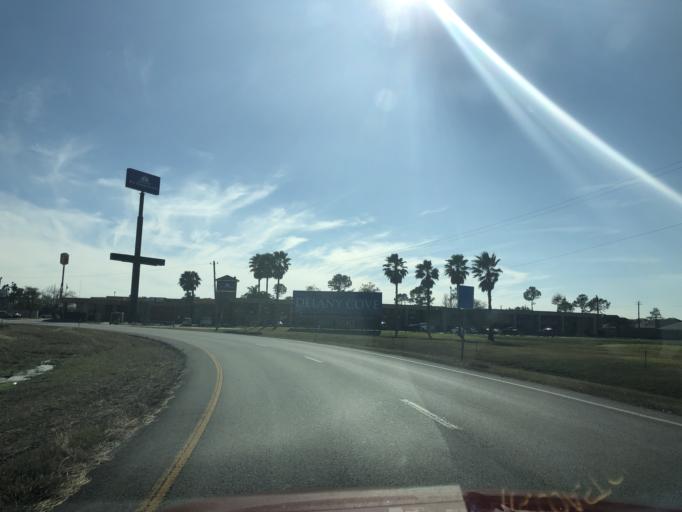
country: US
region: Texas
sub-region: Galveston County
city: Hitchcock
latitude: 29.3891
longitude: -95.0219
